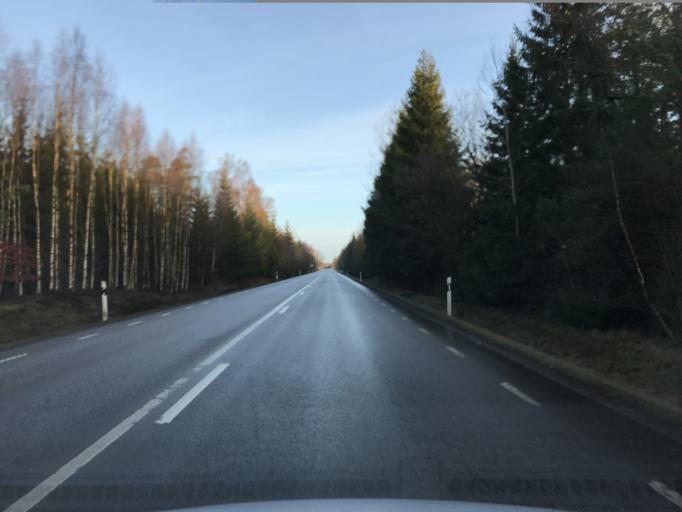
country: SE
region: Skane
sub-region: Hassleholms Kommun
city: Bjarnum
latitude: 56.2455
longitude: 13.7149
